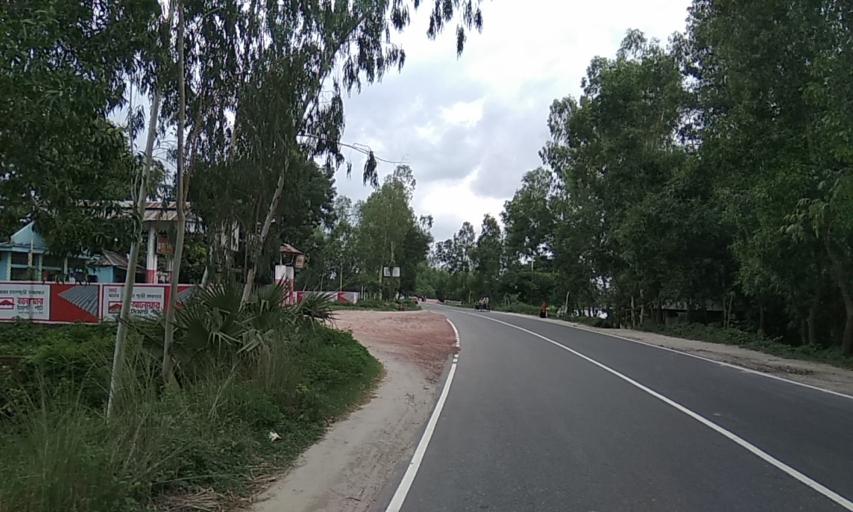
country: BD
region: Rangpur Division
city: Rangpur
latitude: 25.8020
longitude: 89.1831
